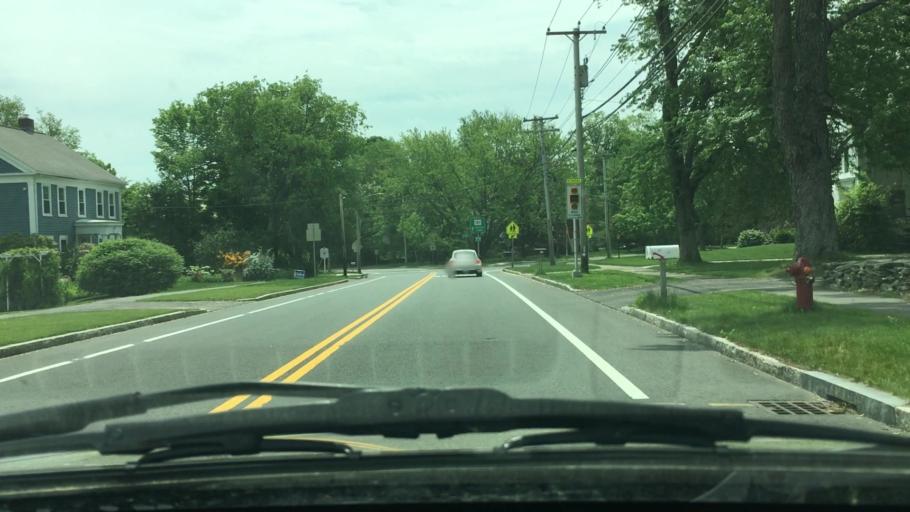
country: US
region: Massachusetts
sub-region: Hampshire County
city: Belchertown
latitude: 42.2741
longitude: -72.3988
